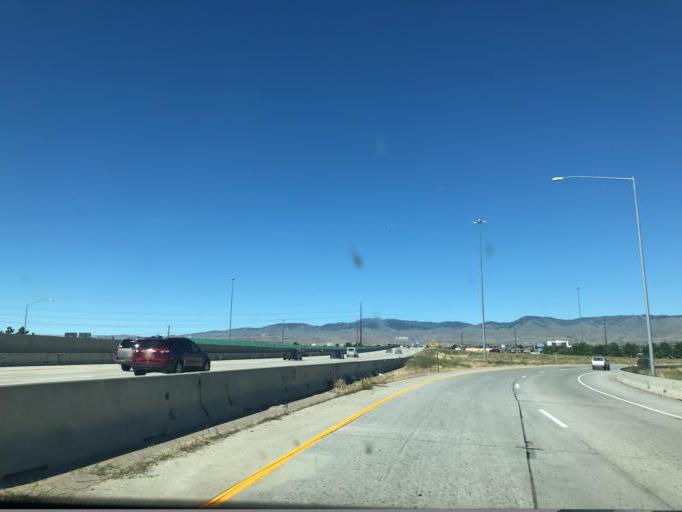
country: US
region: Idaho
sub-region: Ada County
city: Garden City
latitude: 43.6019
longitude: -116.2819
